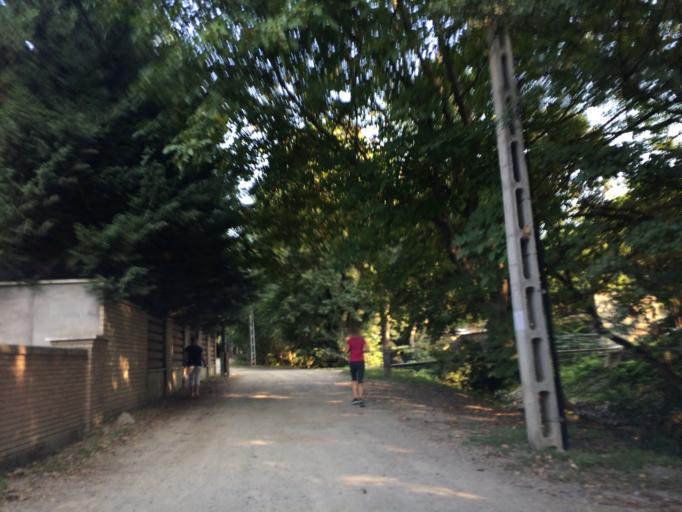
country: HU
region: Pest
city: Szentendre
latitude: 47.6754
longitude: 19.0612
